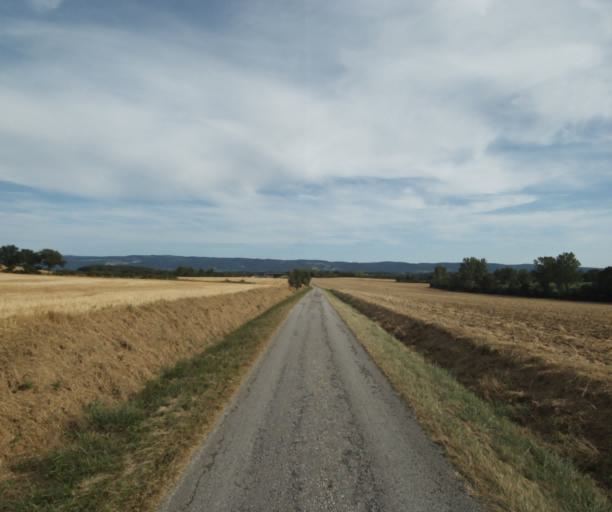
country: FR
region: Midi-Pyrenees
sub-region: Departement du Tarn
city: Puylaurens
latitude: 43.5311
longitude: 2.0357
